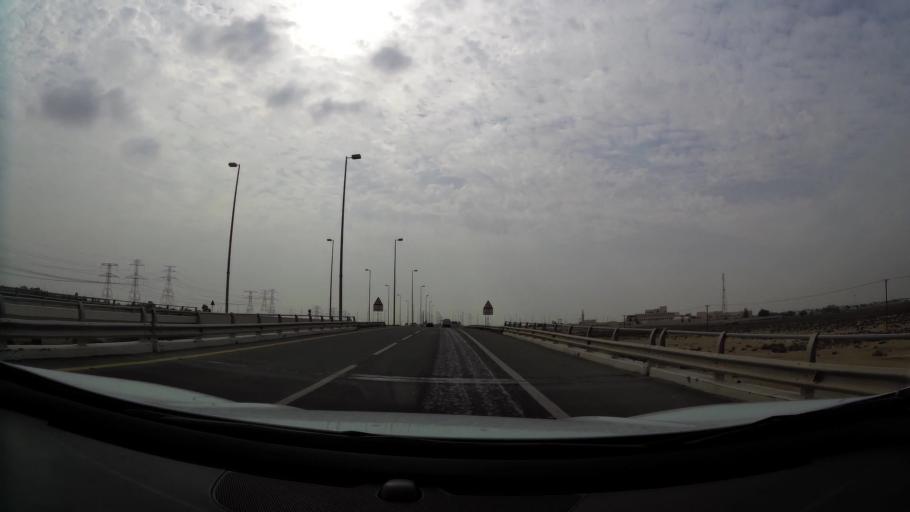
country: AE
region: Abu Dhabi
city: Abu Dhabi
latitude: 24.6625
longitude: 54.7427
